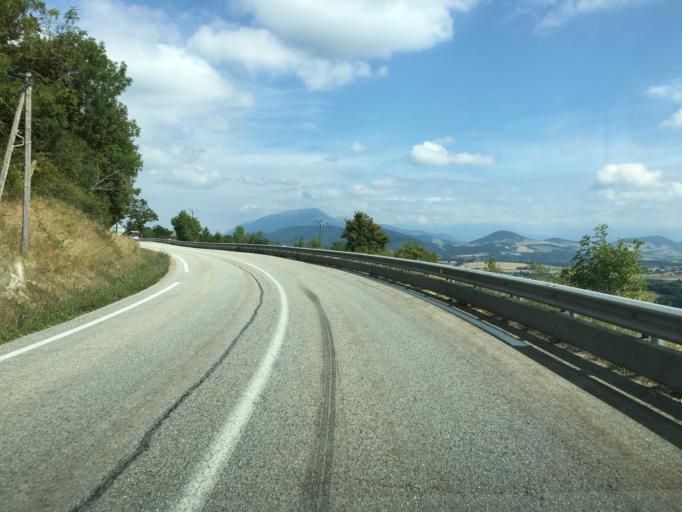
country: FR
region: Rhone-Alpes
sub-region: Departement de l'Isere
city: Mens
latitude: 44.7686
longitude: 5.6625
